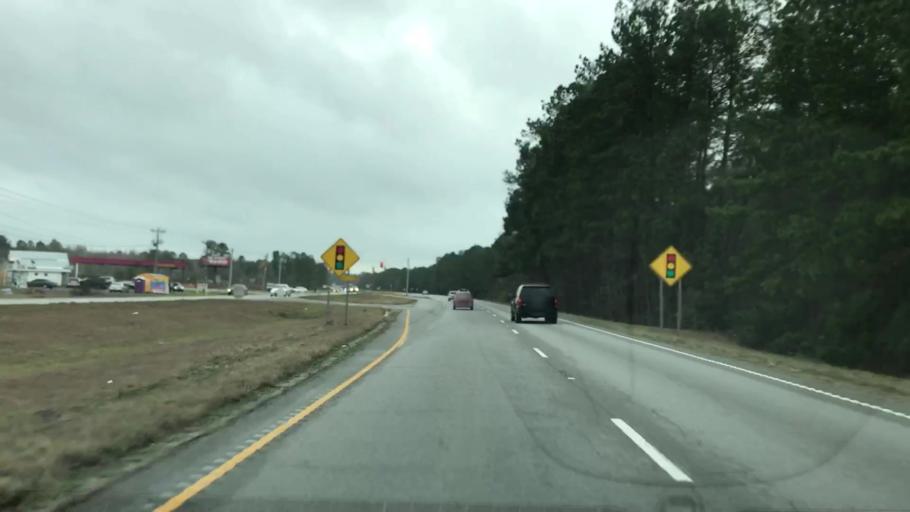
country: US
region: South Carolina
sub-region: Berkeley County
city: Goose Creek
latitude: 33.0607
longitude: -80.0354
